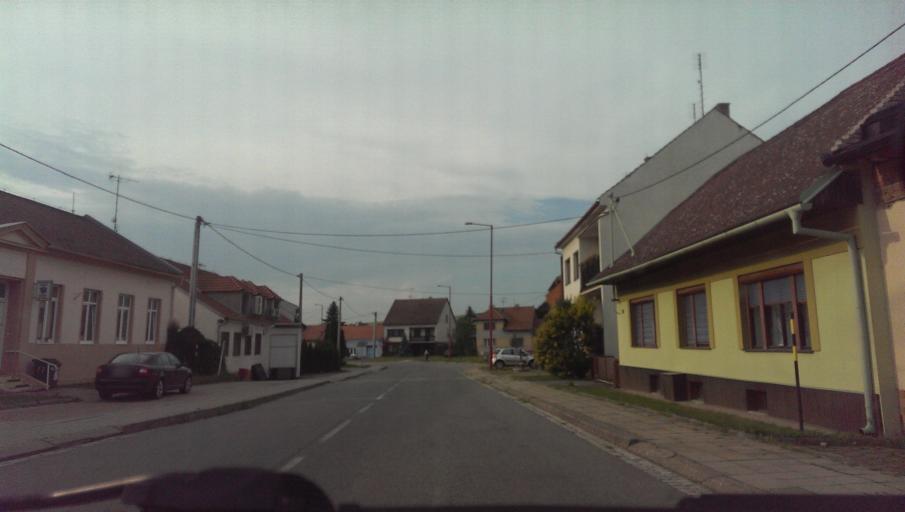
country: CZ
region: Zlin
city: Popovice
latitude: 49.0380
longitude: 17.5047
